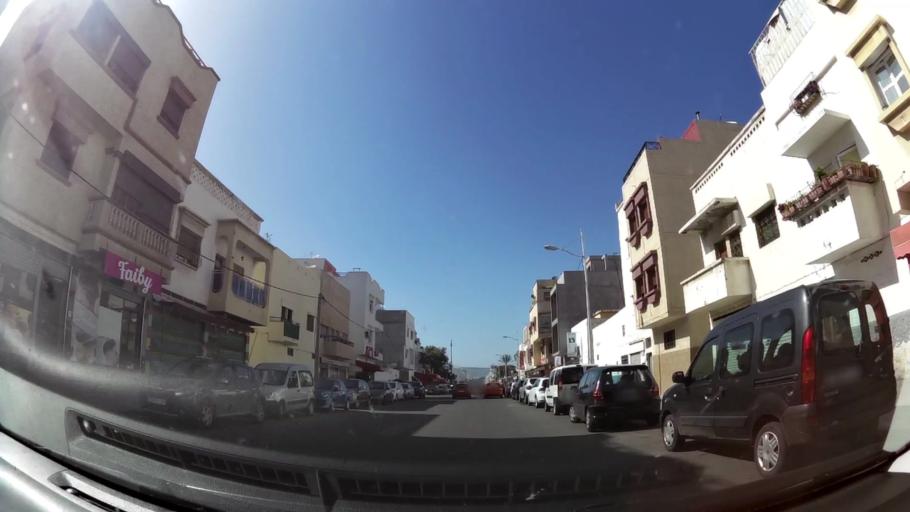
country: MA
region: Souss-Massa-Draa
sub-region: Agadir-Ida-ou-Tnan
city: Agadir
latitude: 30.4116
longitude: -9.5878
